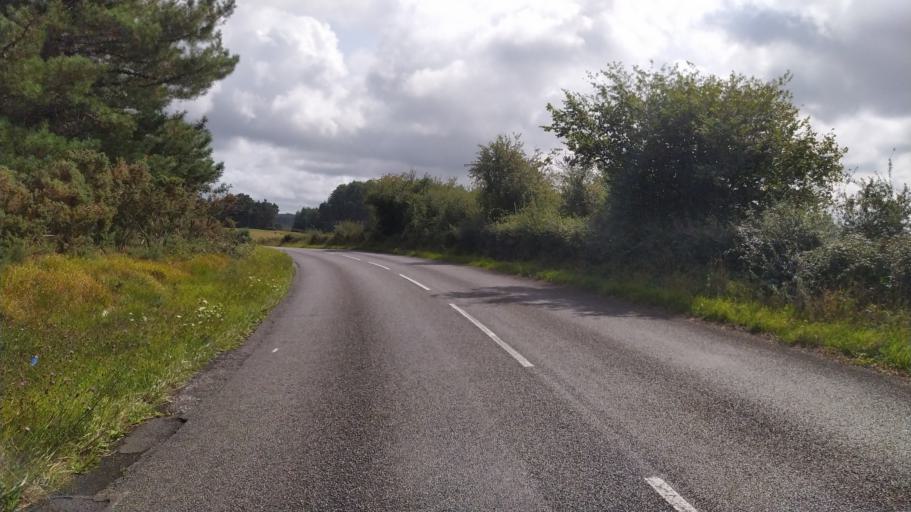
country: GB
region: England
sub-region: Dorset
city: Wareham
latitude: 50.7272
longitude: -2.1179
